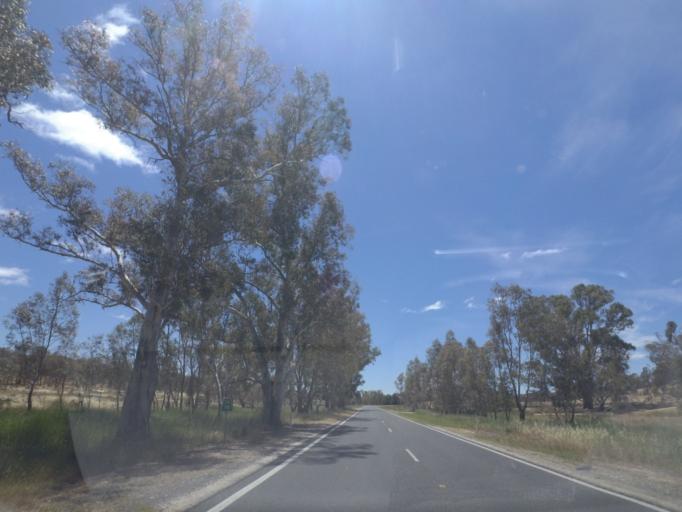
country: AU
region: Victoria
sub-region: Mount Alexander
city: Castlemaine
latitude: -37.1751
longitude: 144.1468
